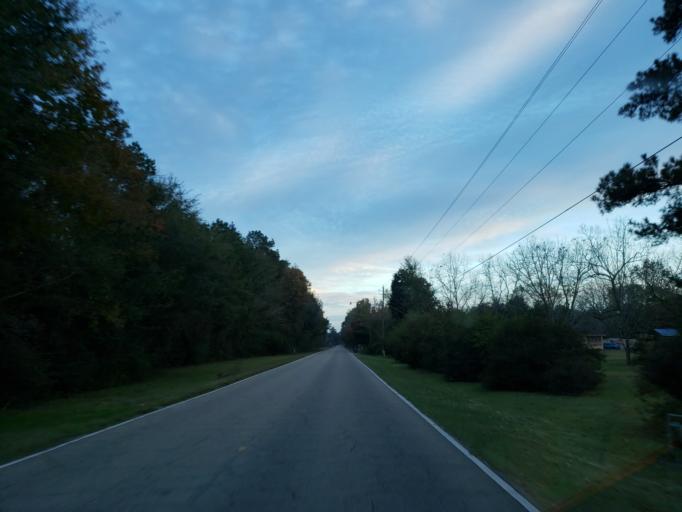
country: US
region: Mississippi
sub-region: Forrest County
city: Hattiesburg
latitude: 31.2857
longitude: -89.2587
